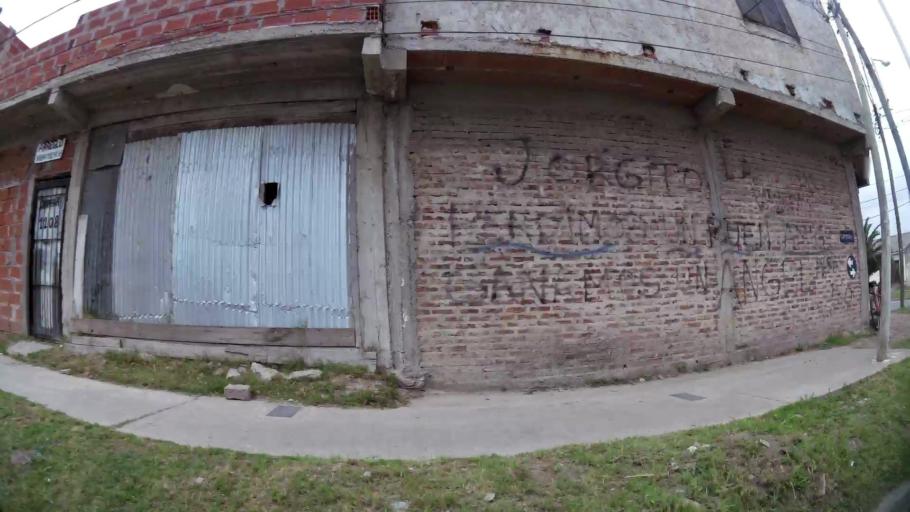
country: AR
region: Buenos Aires
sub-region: Partido de Avellaneda
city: Avellaneda
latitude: -34.6601
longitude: -58.3436
